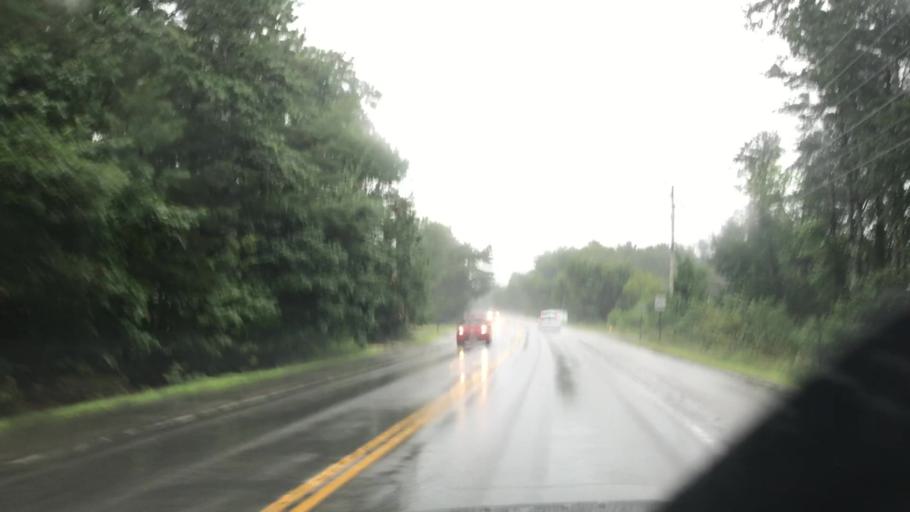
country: US
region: Maine
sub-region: York County
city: Wells Beach Station
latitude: 43.3134
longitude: -70.6527
